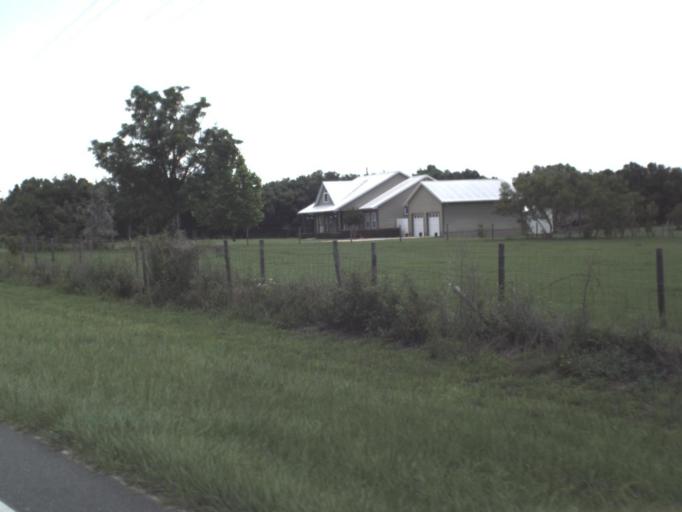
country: US
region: Florida
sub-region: Alachua County
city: Hawthorne
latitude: 29.6781
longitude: -82.0347
